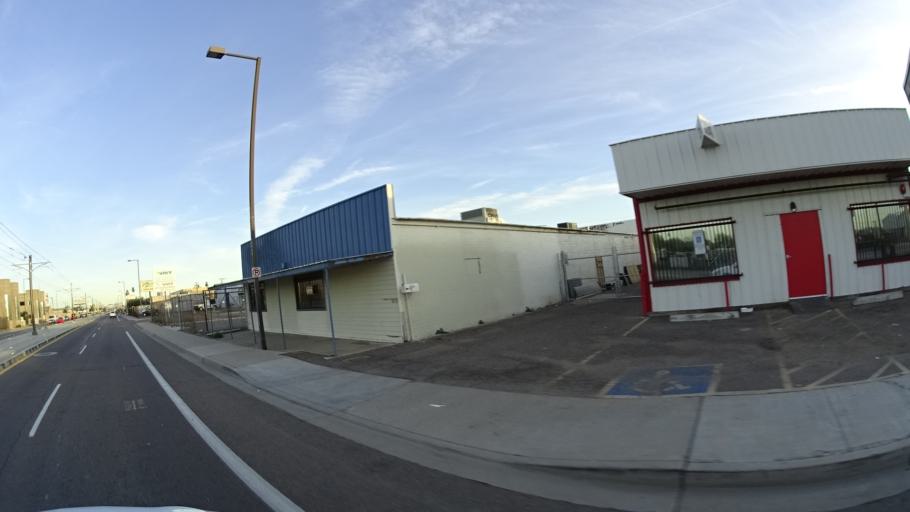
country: US
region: Arizona
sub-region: Maricopa County
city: Phoenix
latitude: 33.4481
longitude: -112.0110
